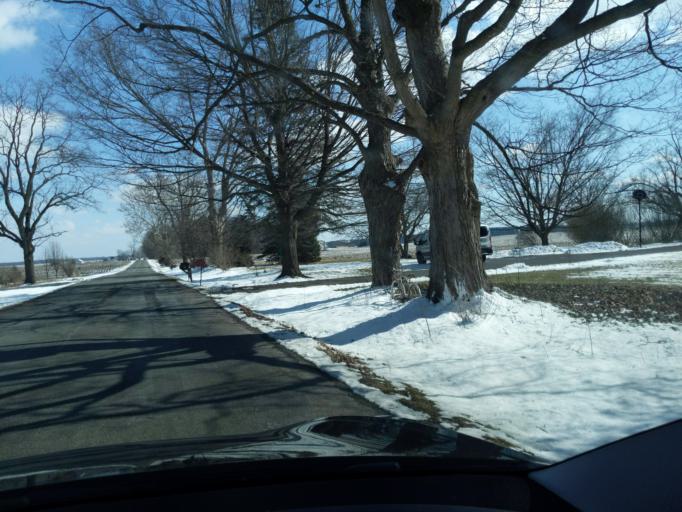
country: US
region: Michigan
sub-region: Ingham County
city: Mason
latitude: 42.6111
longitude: -84.4476
